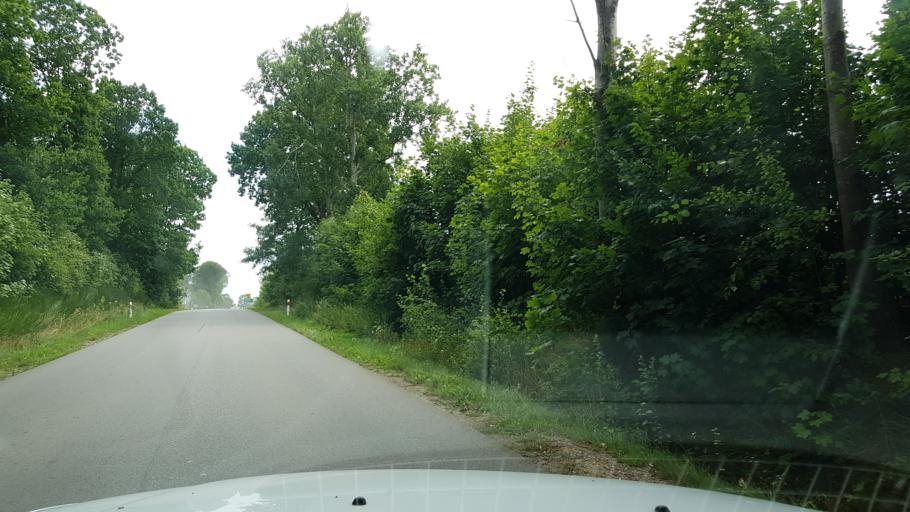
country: PL
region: West Pomeranian Voivodeship
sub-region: Koszalin
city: Koszalin
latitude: 54.1560
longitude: 16.0763
